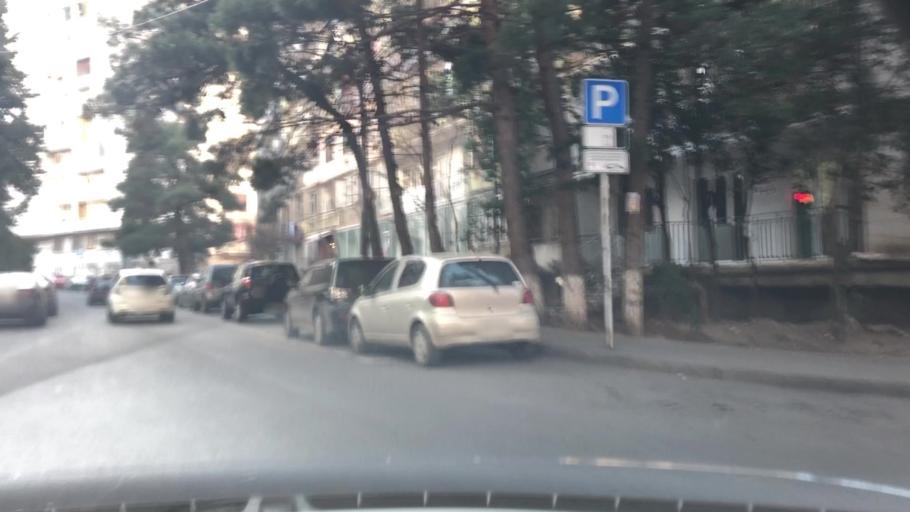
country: GE
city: Tsqnet'i
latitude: 41.7142
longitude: 44.7580
